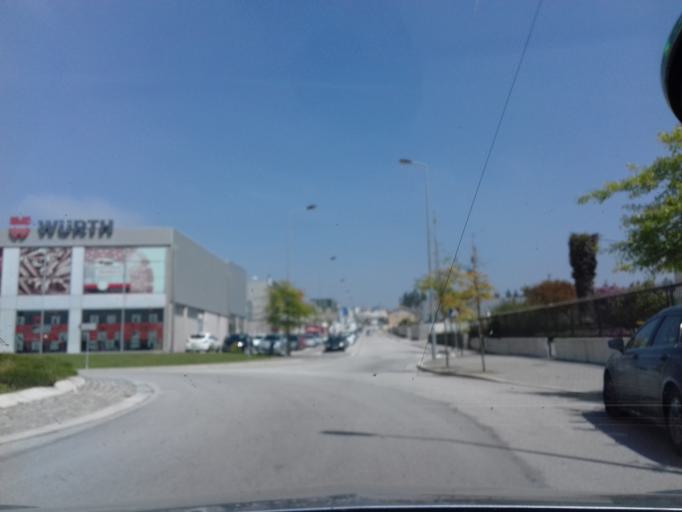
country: PT
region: Porto
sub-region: Vila Nova de Gaia
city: Canelas
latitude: 41.0896
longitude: -8.6040
